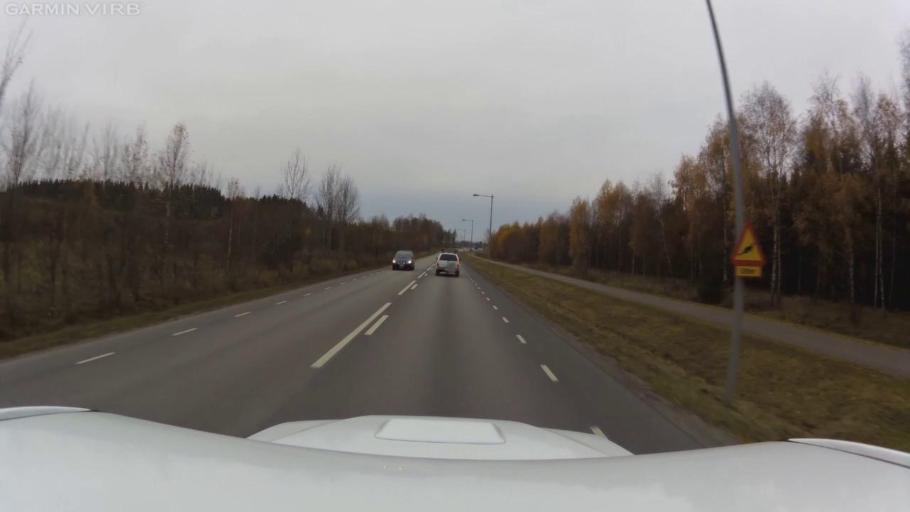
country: SE
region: OEstergoetland
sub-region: Linkopings Kommun
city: Linkoping
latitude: 58.3910
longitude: 15.5963
